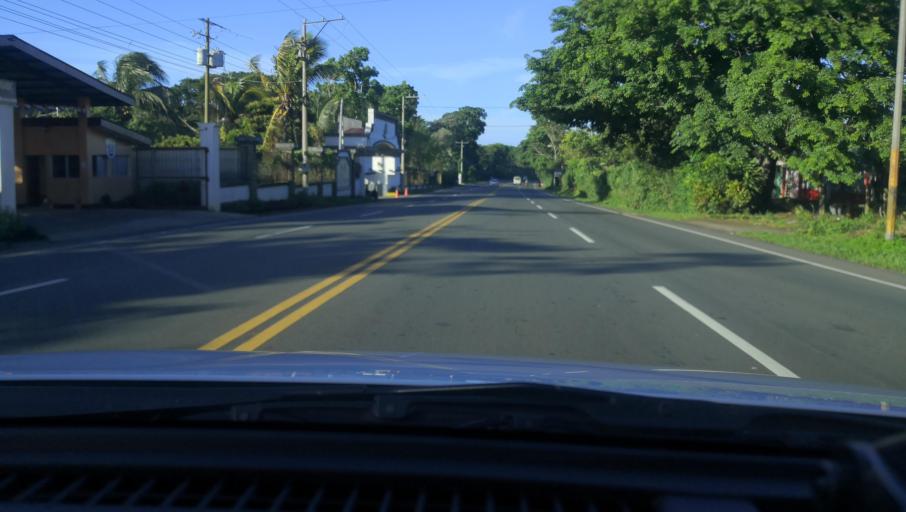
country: NI
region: Carazo
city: Diriamba
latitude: 11.8821
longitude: -86.2358
